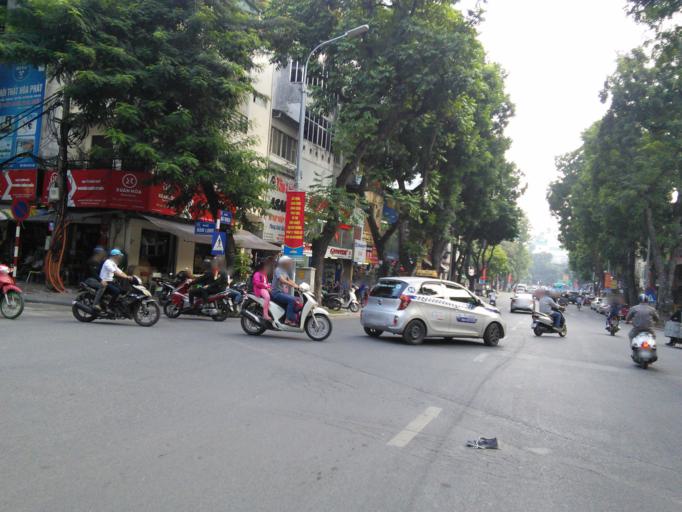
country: VN
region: Ha Noi
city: Hai BaTrung
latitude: 21.0208
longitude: 105.8500
